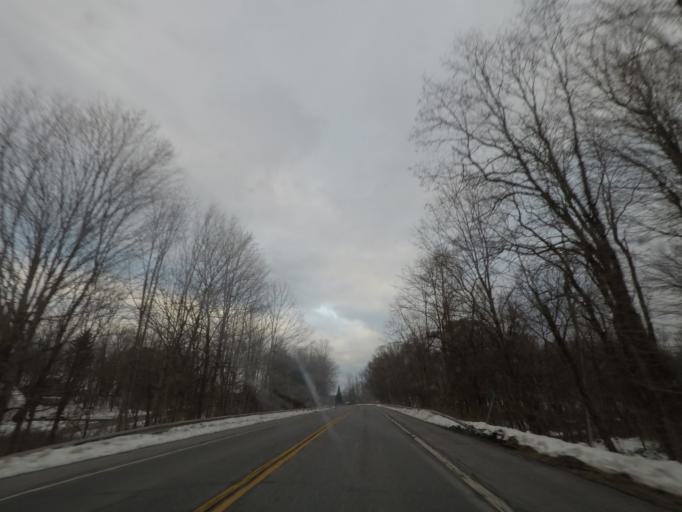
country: US
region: New York
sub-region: Ulster County
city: Plattekill
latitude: 41.6229
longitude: -74.0851
